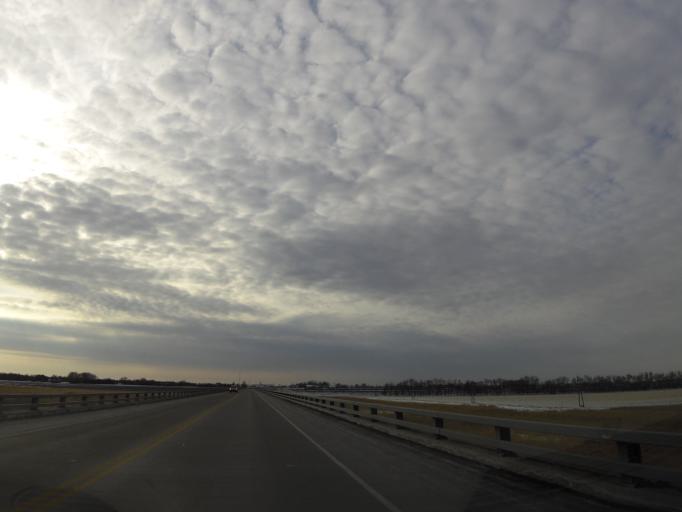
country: US
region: Minnesota
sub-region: Kittson County
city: Hallock
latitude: 48.5720
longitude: -97.1552
